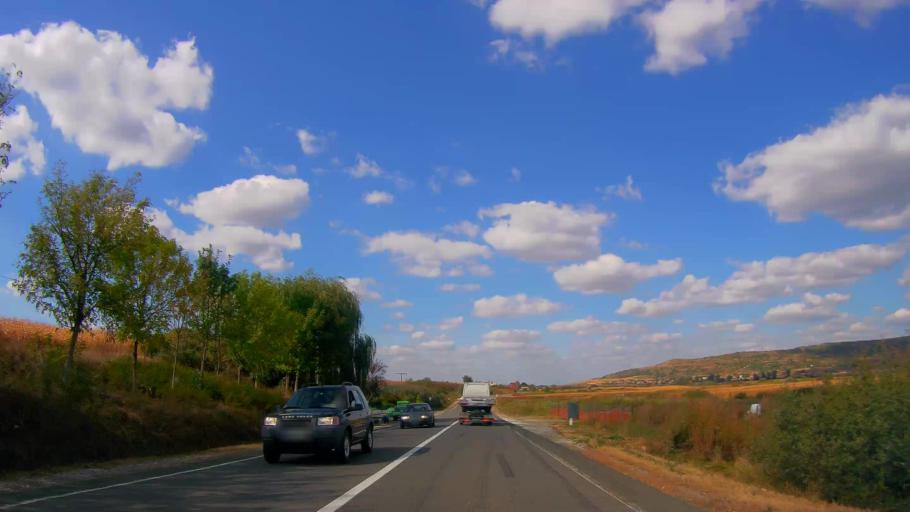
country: RO
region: Salaj
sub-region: Comuna Bobota
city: Dersida
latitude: 47.3712
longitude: 22.7879
